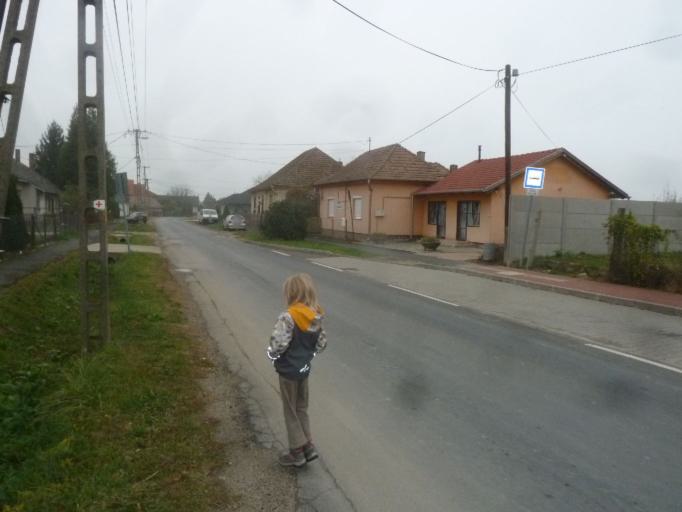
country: HU
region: Zala
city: Pacsa
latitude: 46.6026
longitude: 16.9888
